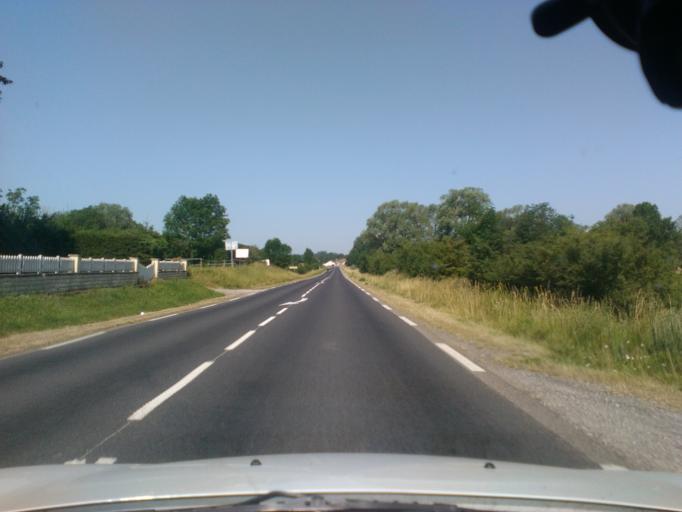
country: FR
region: Lorraine
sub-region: Departement des Vosges
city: Mirecourt
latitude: 48.3074
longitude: 6.1134
